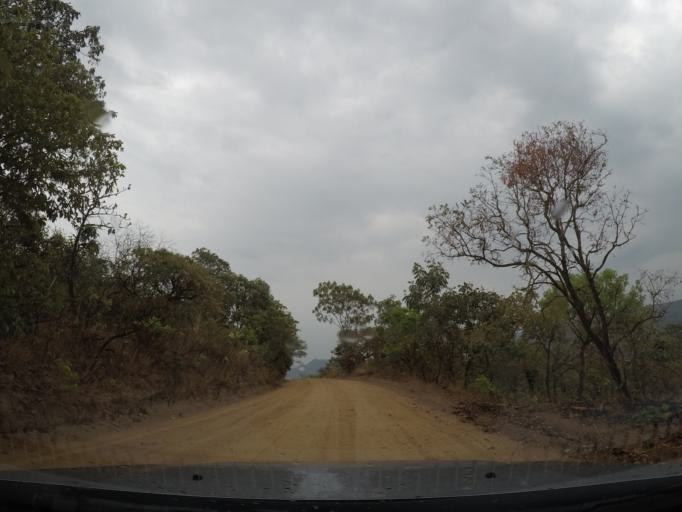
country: BR
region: Goias
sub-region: Pirenopolis
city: Pirenopolis
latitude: -15.8398
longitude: -48.9166
